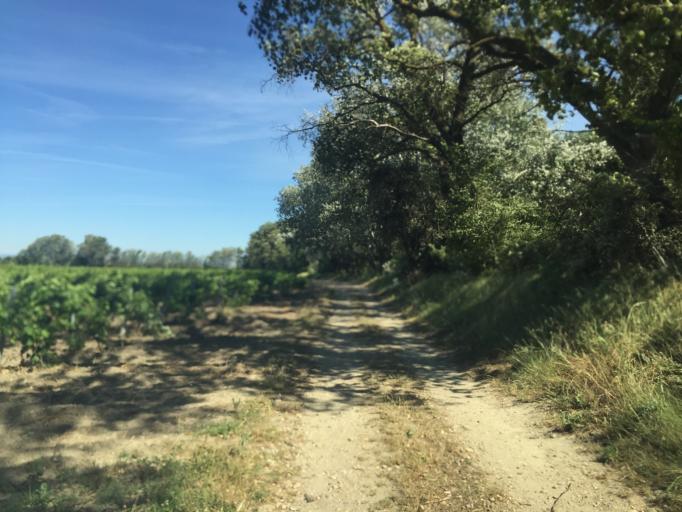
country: FR
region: Provence-Alpes-Cote d'Azur
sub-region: Departement du Vaucluse
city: Chateauneuf-du-Pape
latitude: 44.0444
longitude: 4.8198
